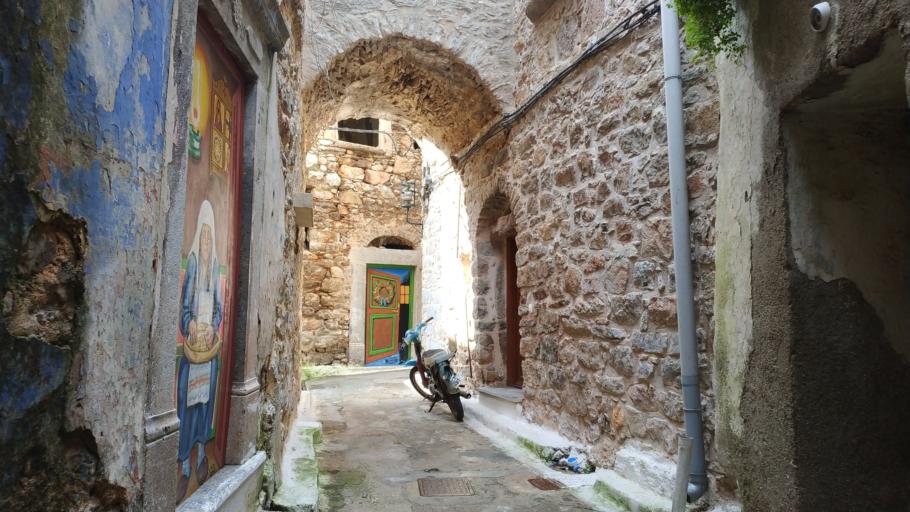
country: GR
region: North Aegean
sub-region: Chios
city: Thymiana
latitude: 38.2468
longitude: 25.9427
